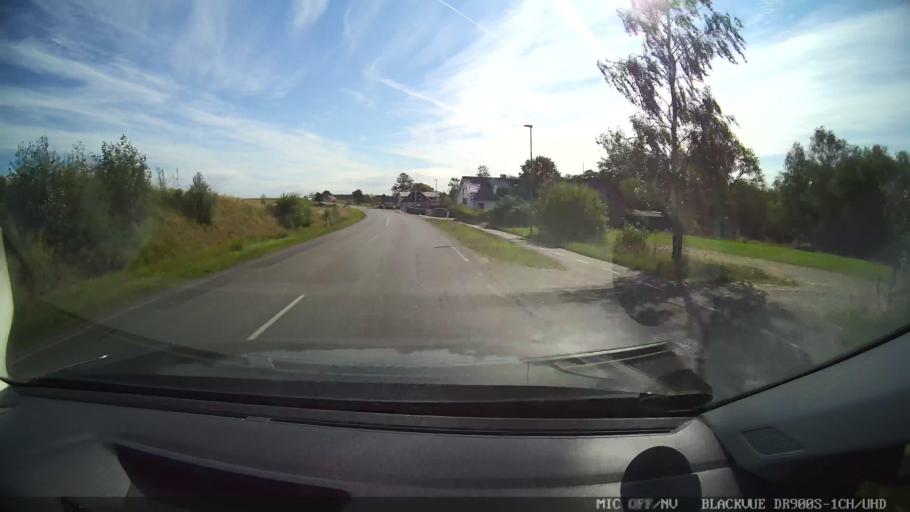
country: DK
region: North Denmark
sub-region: Mariagerfjord Kommune
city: Arden
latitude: 56.7637
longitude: 9.8750
